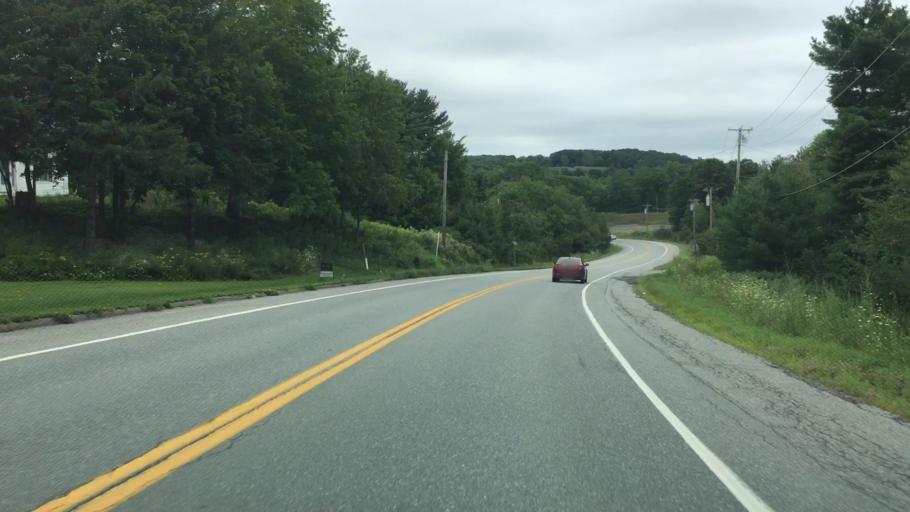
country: US
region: Maine
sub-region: Waldo County
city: Frankfort
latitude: 44.6220
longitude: -68.8703
